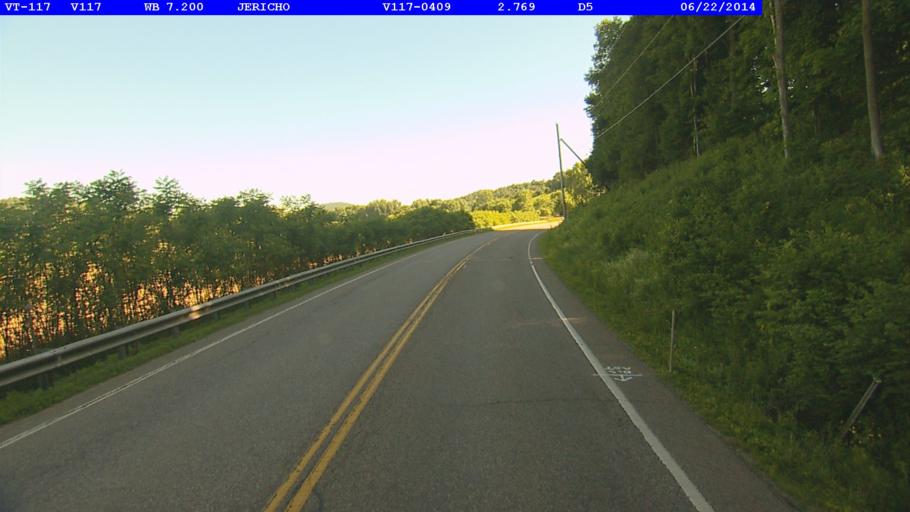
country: US
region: Vermont
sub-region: Chittenden County
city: Williston
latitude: 44.4361
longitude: -73.0210
